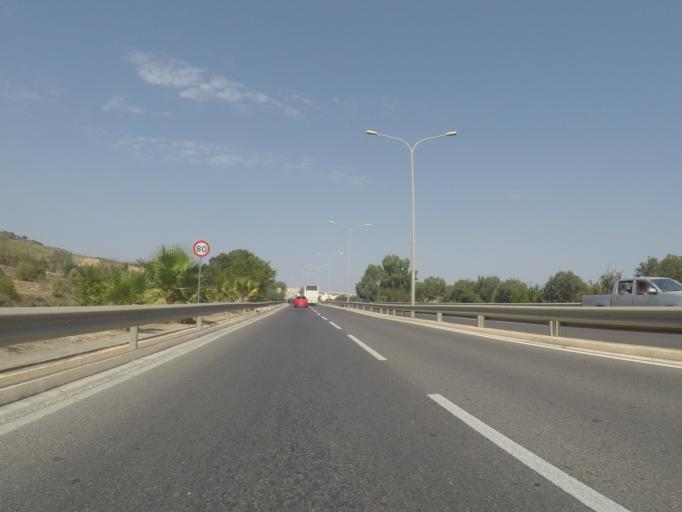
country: MT
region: Saint Paul's Bay
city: San Pawl il-Bahar
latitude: 35.9465
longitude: 14.4025
